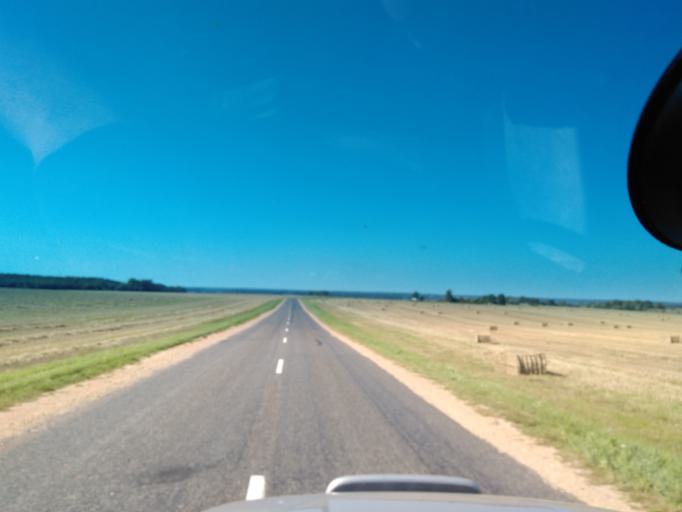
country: BY
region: Minsk
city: Kapyl'
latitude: 53.1920
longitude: 27.0773
